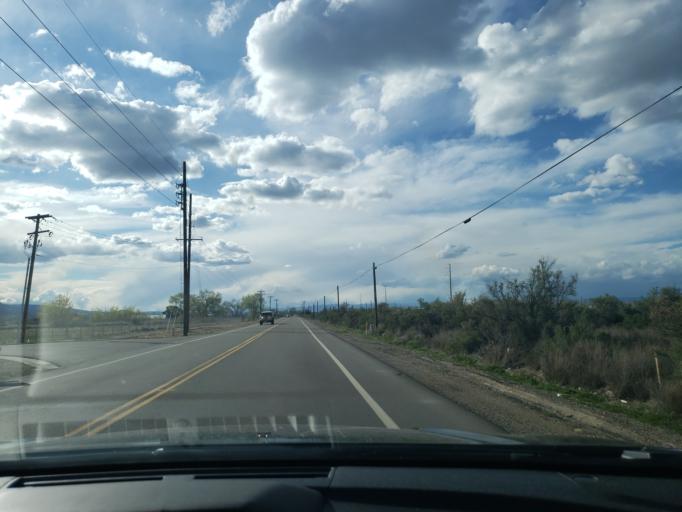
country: US
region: Colorado
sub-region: Mesa County
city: Redlands
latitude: 39.1153
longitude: -108.6565
